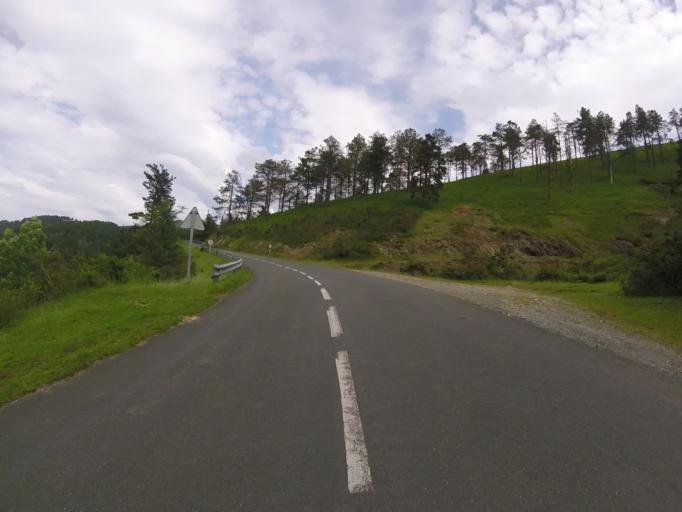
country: ES
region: Navarre
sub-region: Provincia de Navarra
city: Arano
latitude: 43.2450
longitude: -1.8457
